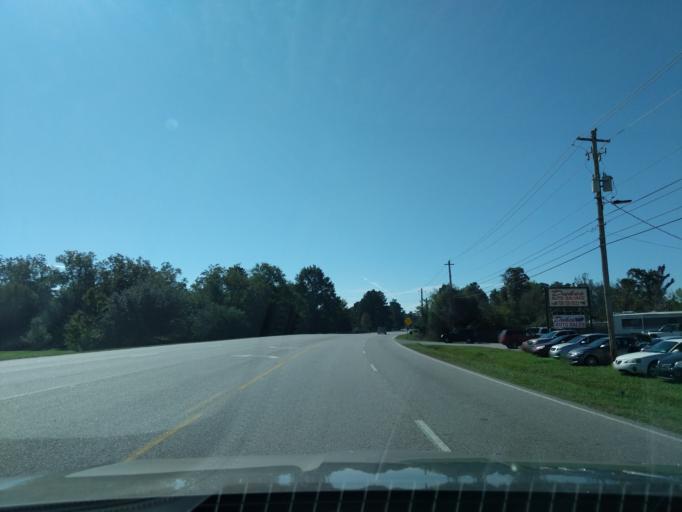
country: US
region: Georgia
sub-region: Richmond County
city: Augusta
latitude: 33.4246
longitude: -82.0062
